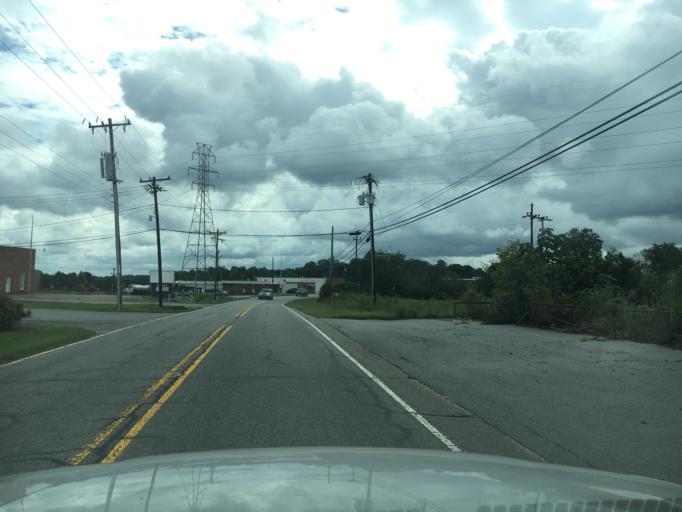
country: US
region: North Carolina
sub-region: Catawba County
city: Saint Stephens
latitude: 35.7275
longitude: -81.2716
